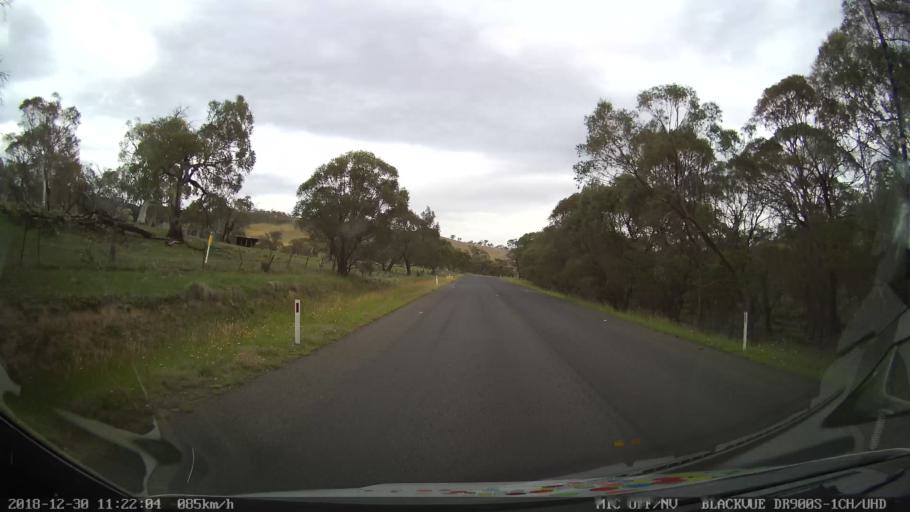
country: AU
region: New South Wales
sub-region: Snowy River
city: Jindabyne
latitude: -36.5044
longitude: 148.6713
